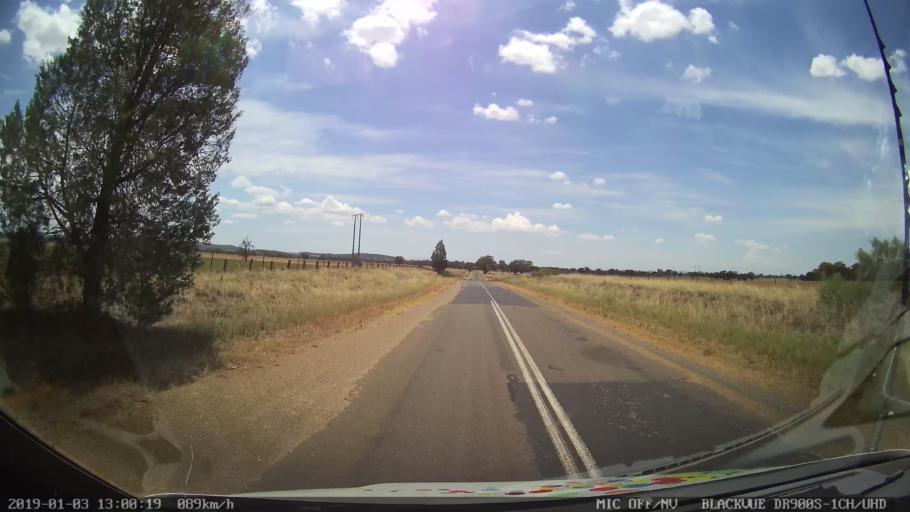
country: AU
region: New South Wales
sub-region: Cabonne
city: Canowindra
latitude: -33.6314
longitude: 148.4018
